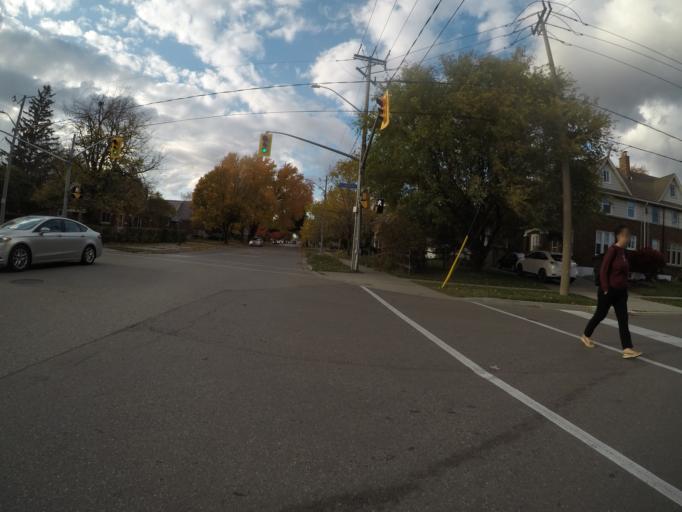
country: CA
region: Ontario
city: Waterloo
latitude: 43.4522
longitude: -80.5076
